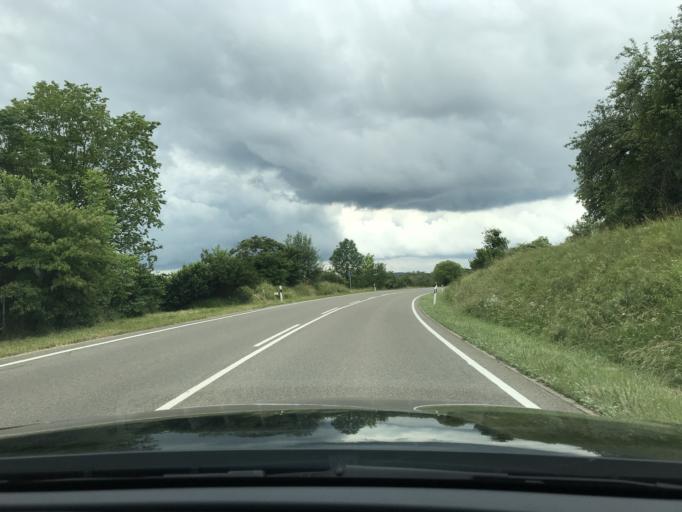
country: DE
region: Baden-Wuerttemberg
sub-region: Regierungsbezirk Stuttgart
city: Korb
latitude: 48.8506
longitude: 9.3515
